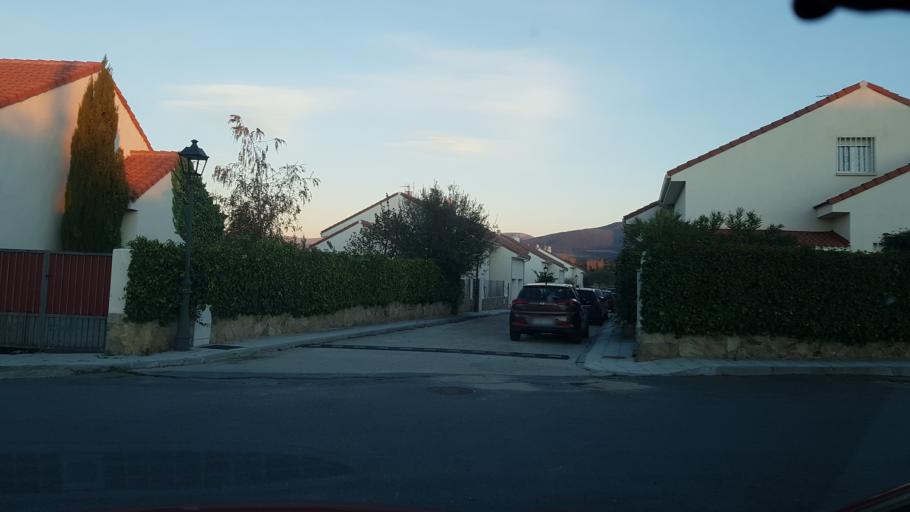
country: ES
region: Castille and Leon
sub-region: Provincia de Segovia
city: Ortigosa del Monte
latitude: 40.8511
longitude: -4.1625
